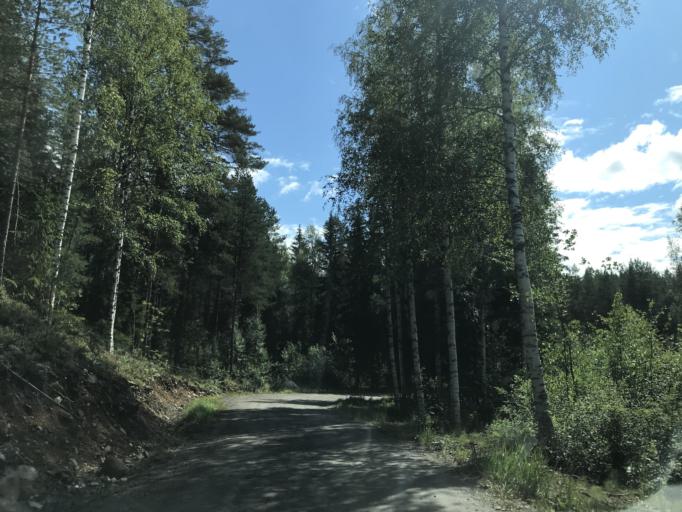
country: FI
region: Haeme
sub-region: Forssa
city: Tammela
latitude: 60.6282
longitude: 23.7575
